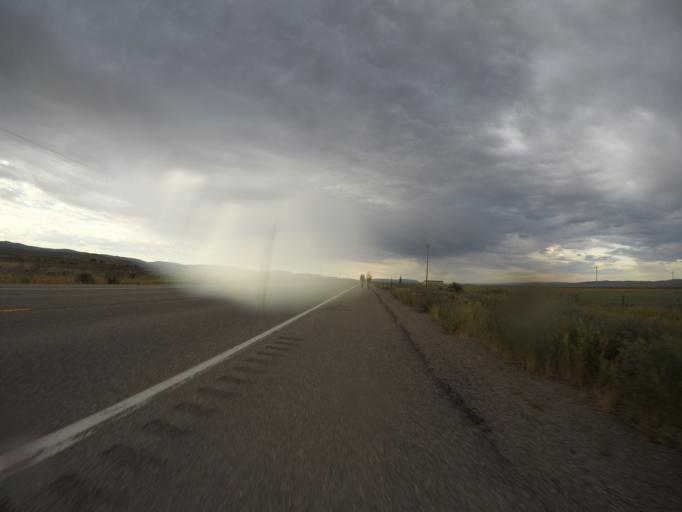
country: US
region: Utah
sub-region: Rich County
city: Randolph
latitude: 41.9367
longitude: -110.9533
